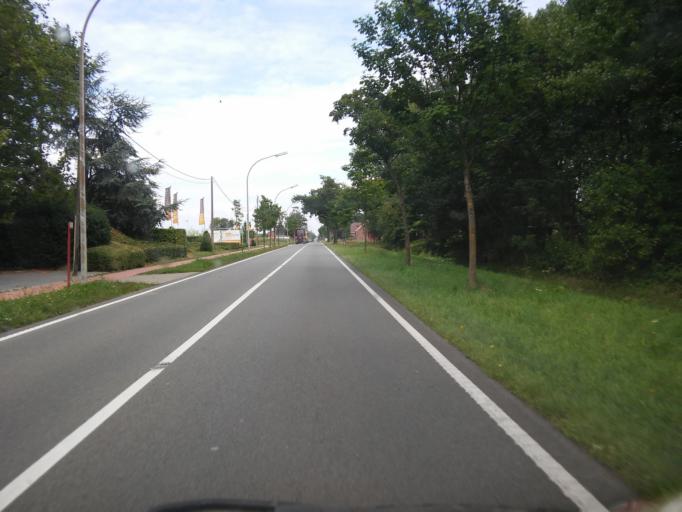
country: BE
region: Flanders
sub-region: Provincie Antwerpen
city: Puurs
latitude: 51.0471
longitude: 4.2860
